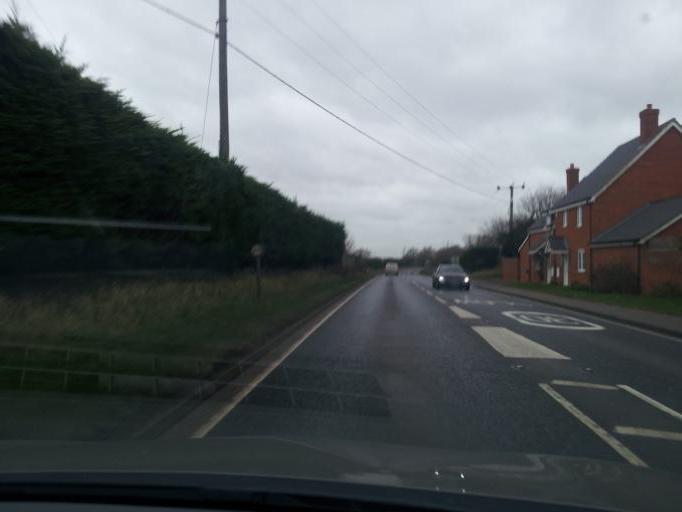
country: GB
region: England
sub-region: Suffolk
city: Botesdale
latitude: 52.3511
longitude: 1.0539
